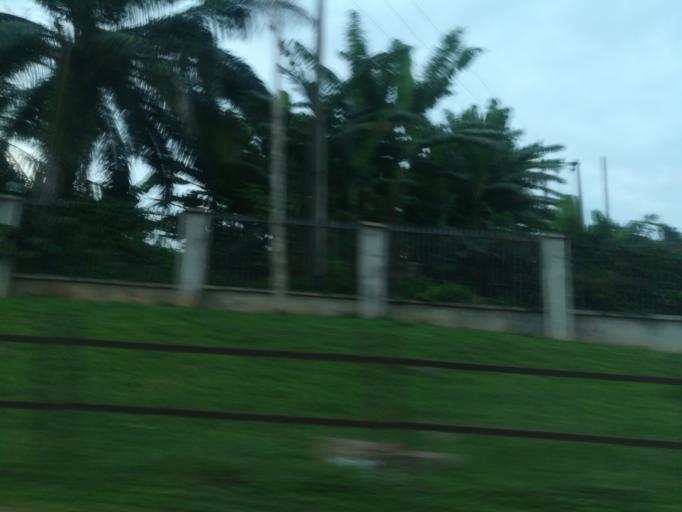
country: NG
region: Oyo
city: Ibadan
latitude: 7.4196
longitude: 3.9104
